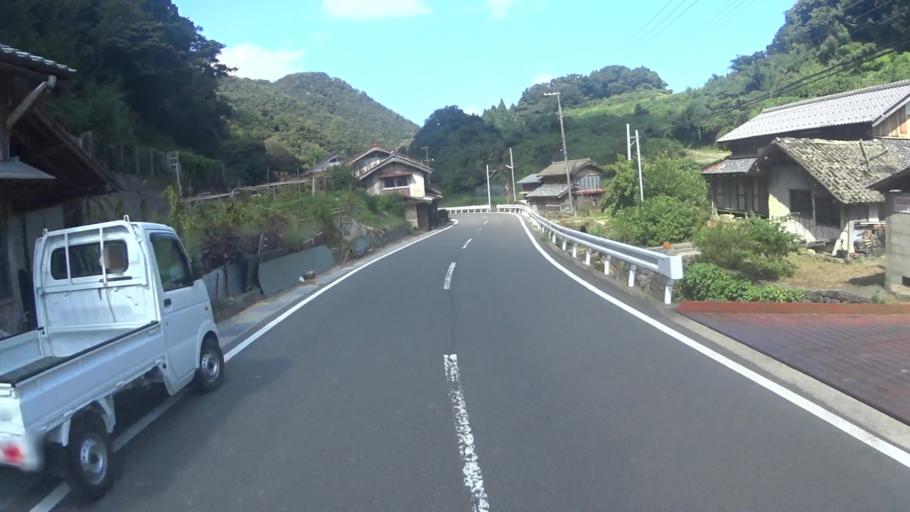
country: JP
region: Kyoto
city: Miyazu
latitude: 35.6979
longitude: 135.2785
